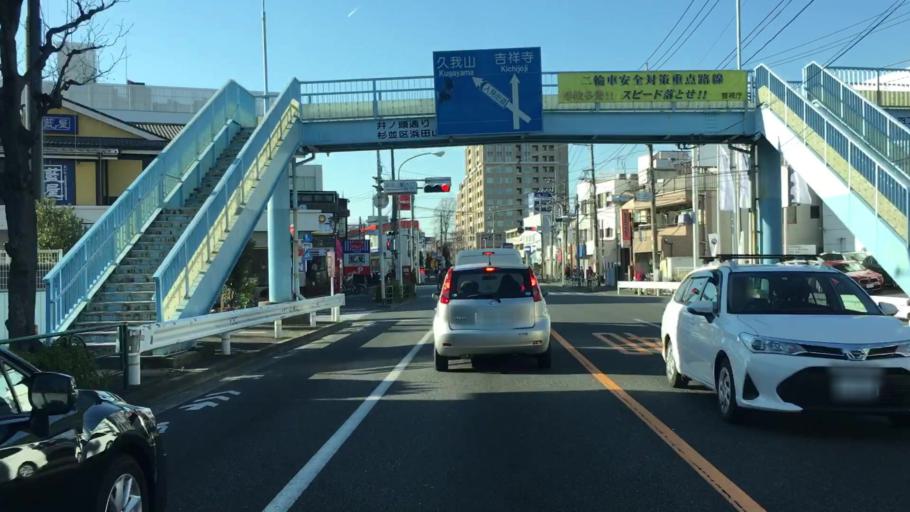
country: JP
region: Tokyo
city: Tokyo
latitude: 35.6841
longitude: 139.6281
